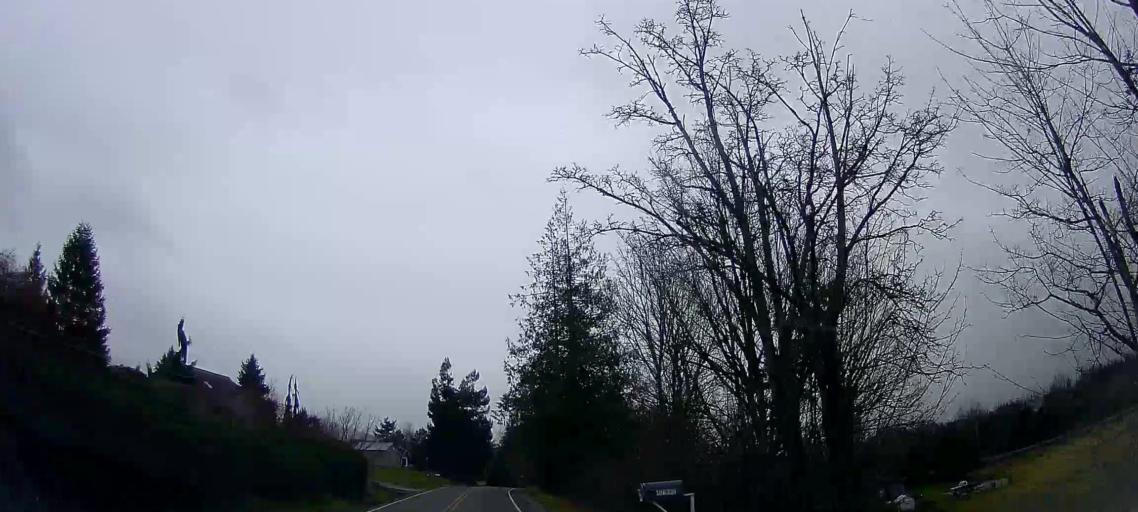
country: US
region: Washington
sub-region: Skagit County
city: Mount Vernon
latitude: 48.3860
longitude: -122.3220
